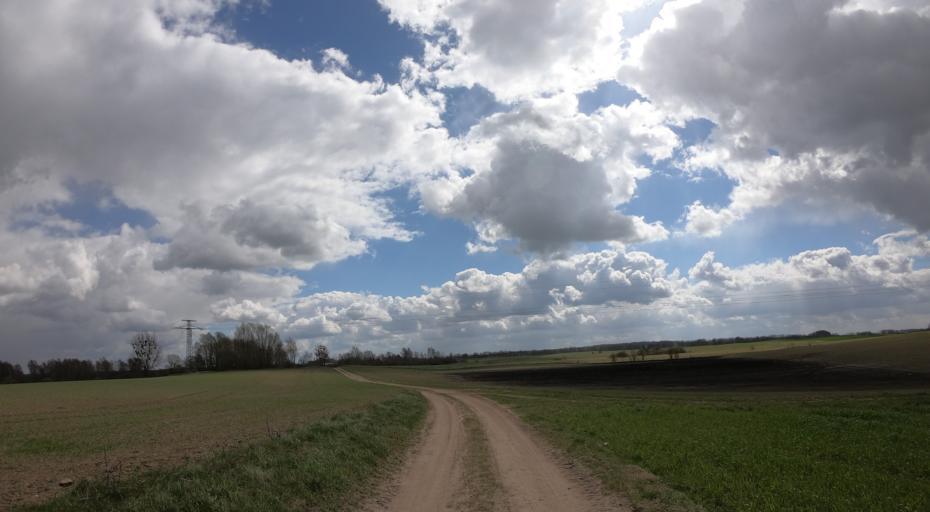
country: PL
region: West Pomeranian Voivodeship
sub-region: Powiat drawski
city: Drawsko Pomorskie
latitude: 53.5485
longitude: 15.8589
